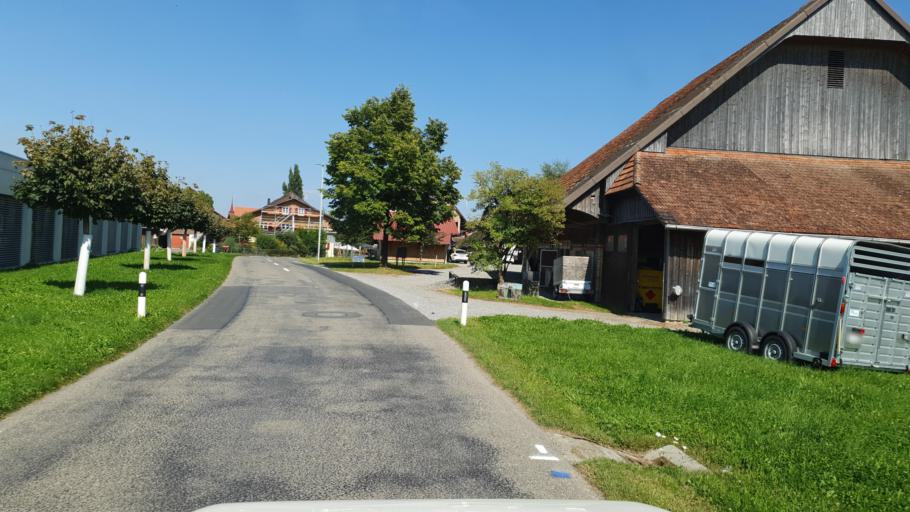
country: CH
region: Aargau
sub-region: Bezirk Muri
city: Oberruti
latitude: 47.1585
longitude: 8.3682
